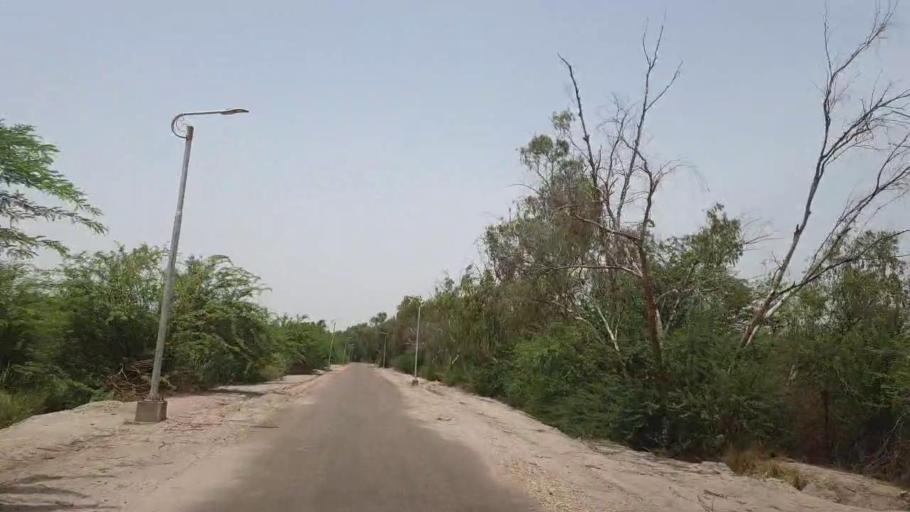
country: PK
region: Sindh
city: Sakrand
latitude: 26.0998
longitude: 68.2466
